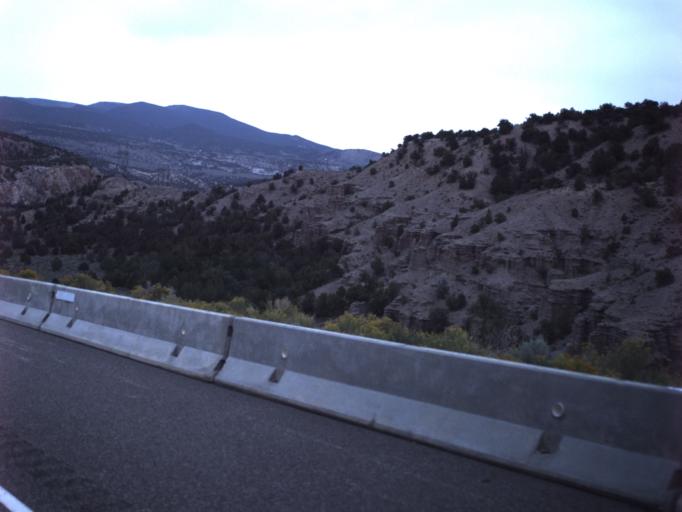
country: US
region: Utah
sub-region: Sevier County
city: Monroe
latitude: 38.5568
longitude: -112.3627
